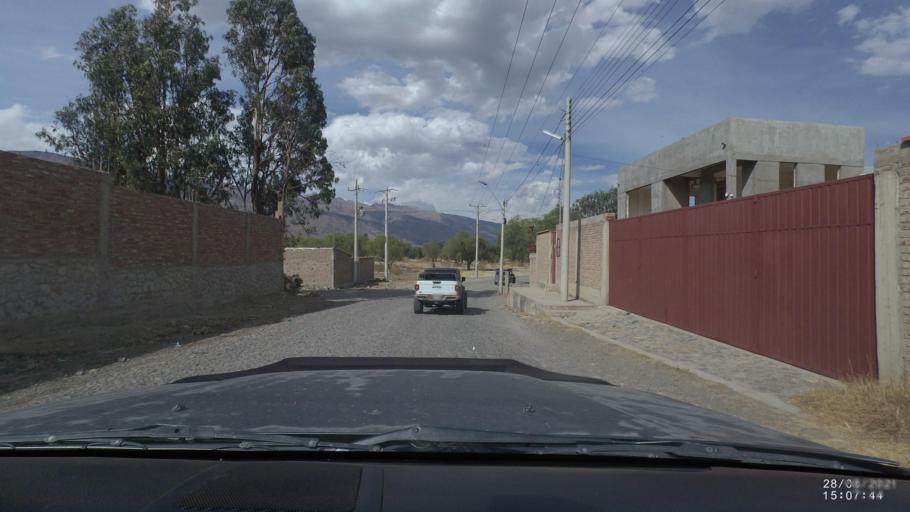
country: BO
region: Cochabamba
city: Cochabamba
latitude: -17.3367
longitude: -66.2797
